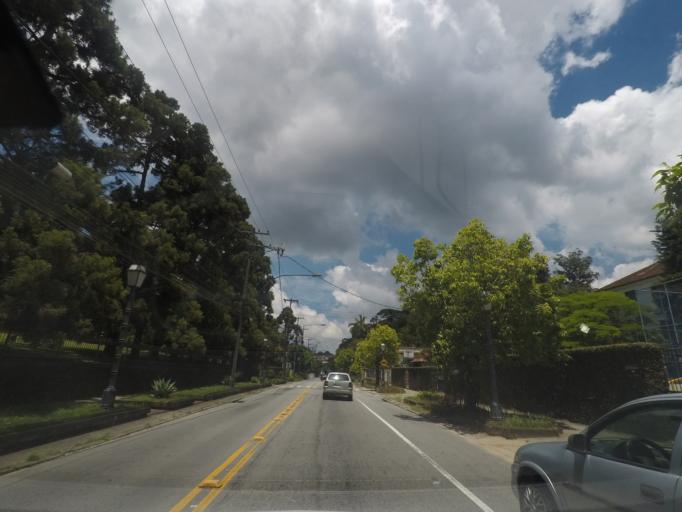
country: BR
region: Rio de Janeiro
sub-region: Petropolis
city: Petropolis
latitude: -22.5042
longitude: -43.1755
